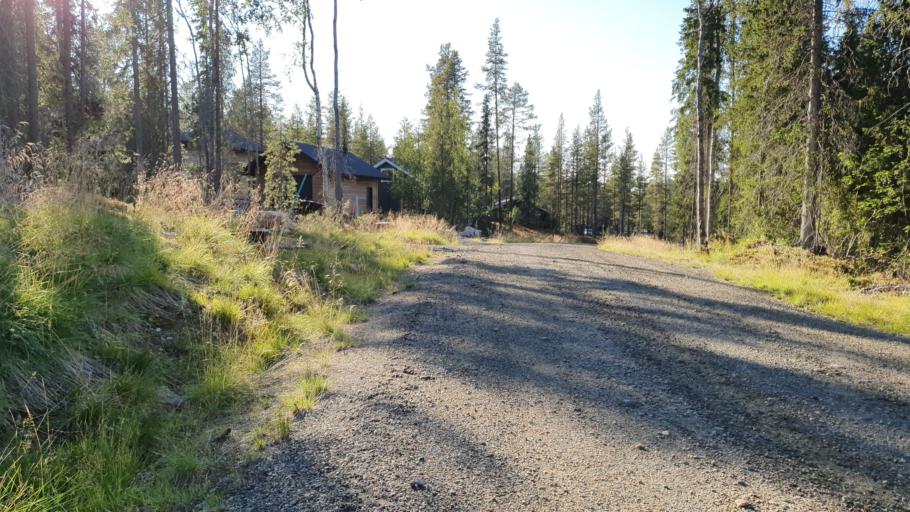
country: FI
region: Lapland
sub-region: Tunturi-Lappi
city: Kolari
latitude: 67.5981
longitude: 24.1997
